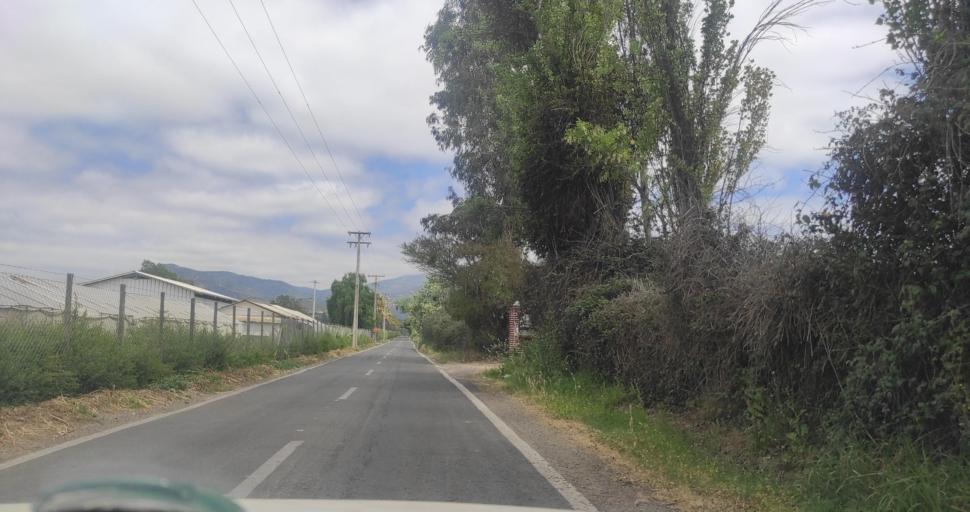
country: CL
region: Valparaiso
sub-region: Provincia de Marga Marga
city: Limache
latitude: -33.0269
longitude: -71.2290
